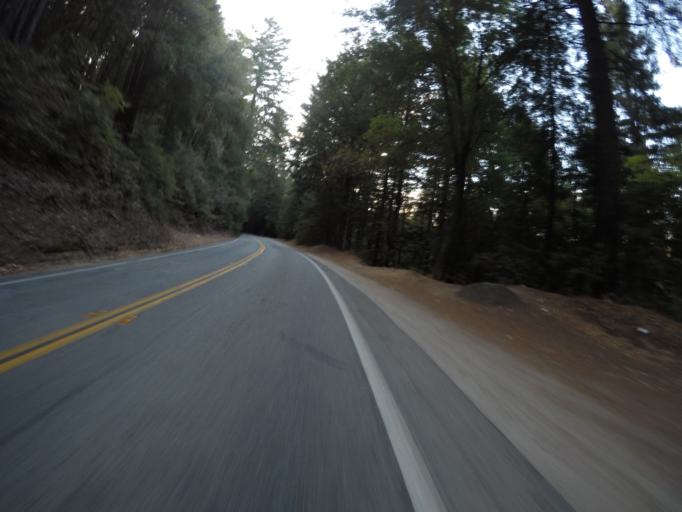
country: US
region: California
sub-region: Santa Cruz County
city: Mount Hermon
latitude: 37.0304
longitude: -122.0592
